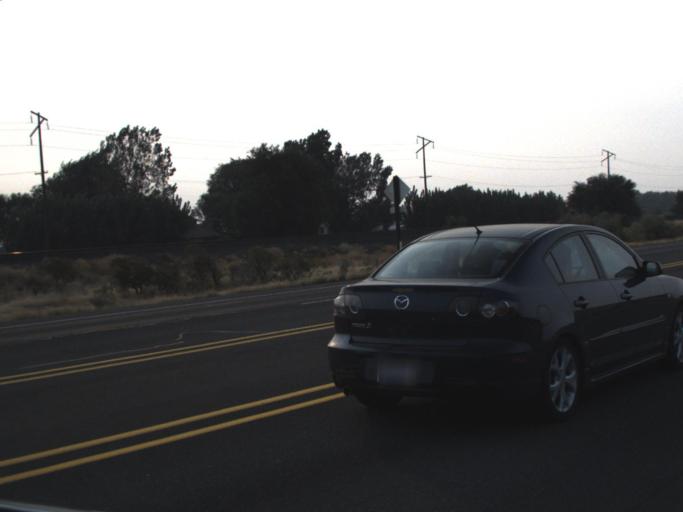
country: US
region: Washington
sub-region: Yakima County
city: Wapato
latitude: 46.4903
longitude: -120.4569
